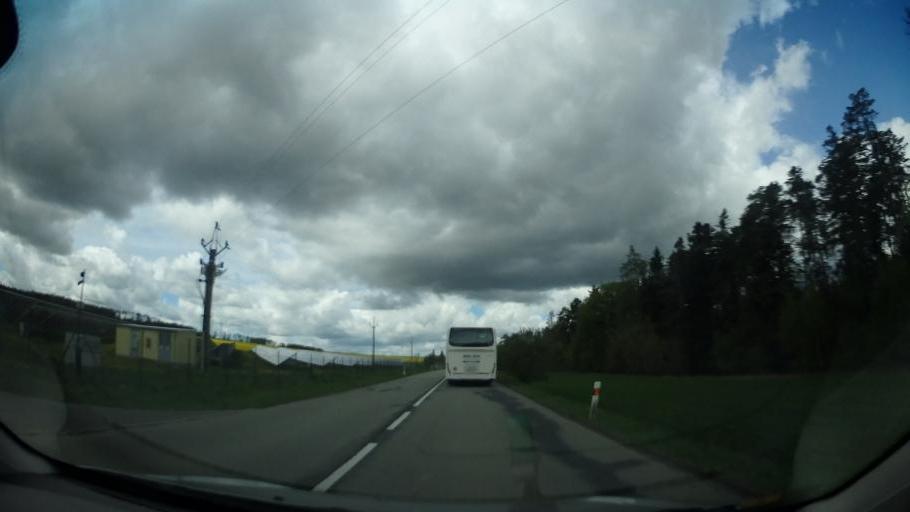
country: CZ
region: Vysocina
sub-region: Okres Zd'ar nad Sazavou
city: Velka Bites
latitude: 49.2748
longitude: 16.2725
